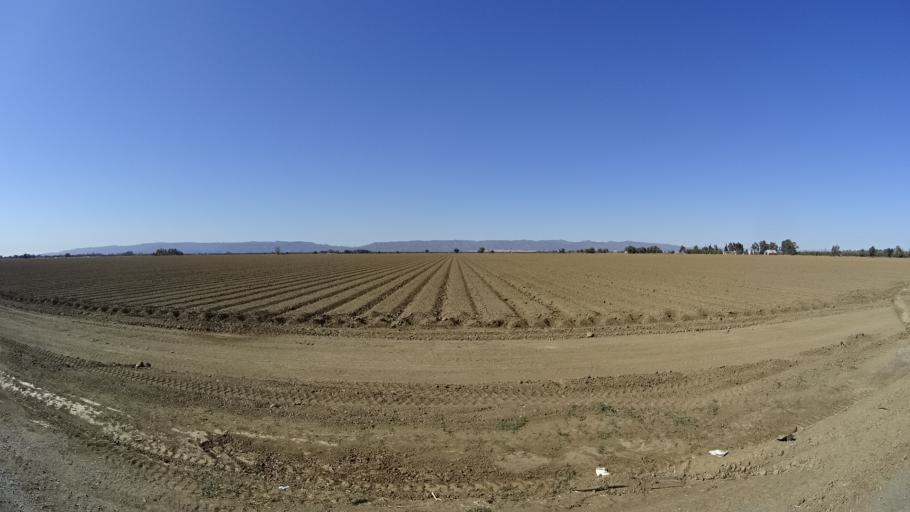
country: US
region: California
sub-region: Solano County
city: Dixon
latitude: 38.5567
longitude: -121.8580
